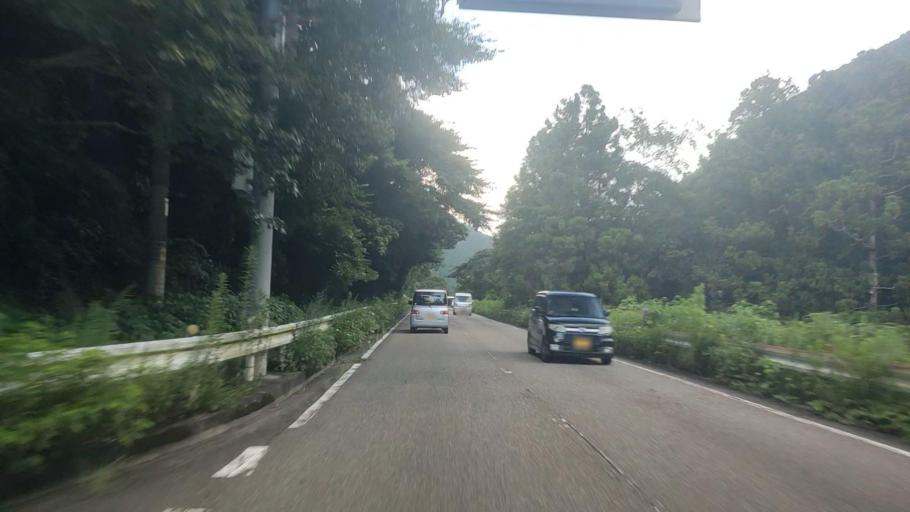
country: JP
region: Wakayama
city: Tanabe
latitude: 33.7638
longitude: 135.5004
